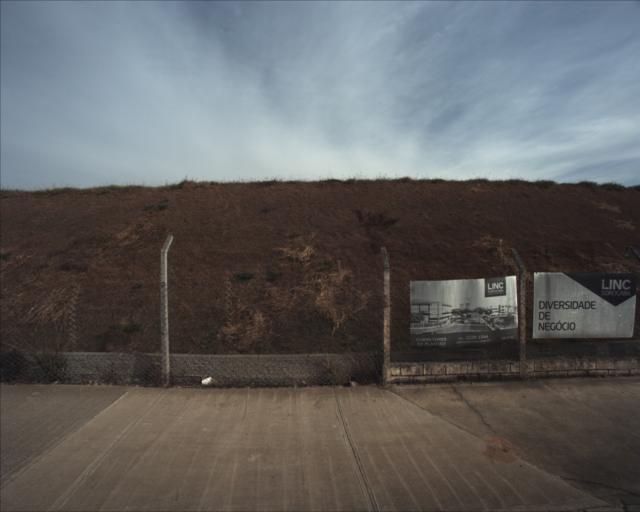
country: BR
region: Sao Paulo
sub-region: Sorocaba
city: Sorocaba
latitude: -23.4566
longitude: -47.4520
